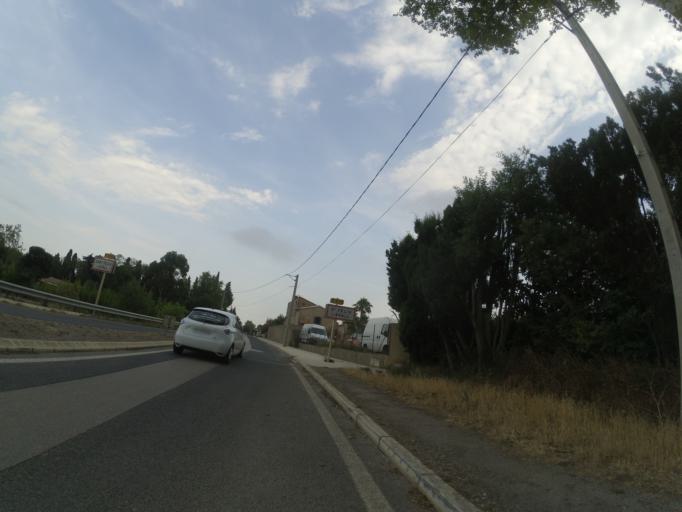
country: FR
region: Languedoc-Roussillon
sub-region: Departement des Pyrenees-Orientales
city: Corneilla-la-Riviere
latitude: 42.6843
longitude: 2.7294
